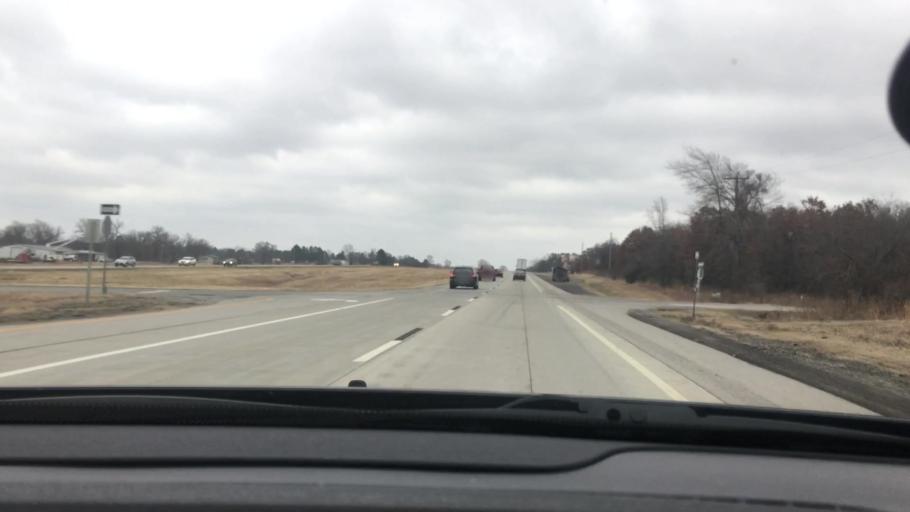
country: US
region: Oklahoma
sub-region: Atoka County
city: Atoka
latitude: 34.2003
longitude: -96.2381
